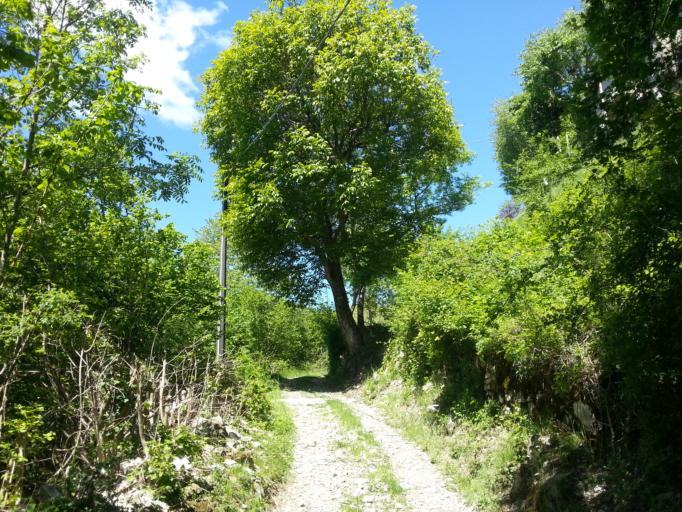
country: IT
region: Lombardy
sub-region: Provincia di Como
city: Ossuccio
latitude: 45.9931
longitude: 9.1748
